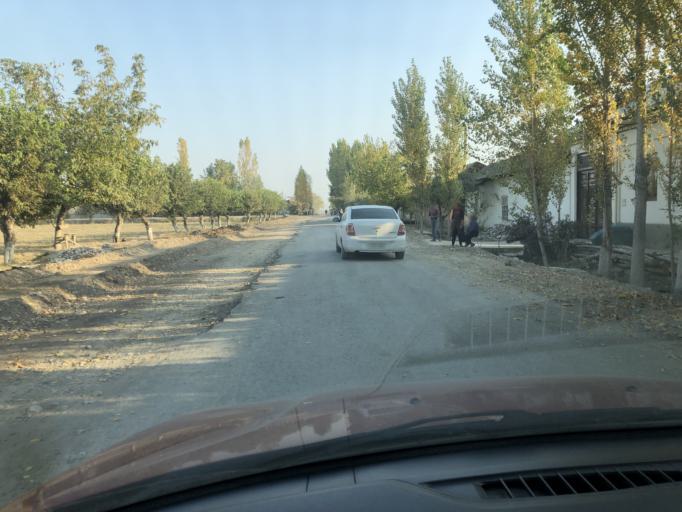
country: UZ
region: Namangan
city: Uychi
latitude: 41.0650
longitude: 71.9868
